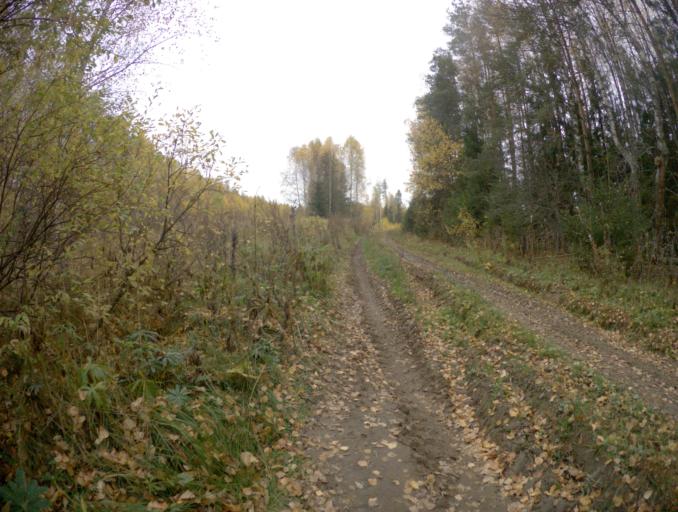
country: RU
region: Vladimir
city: Golovino
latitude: 55.9372
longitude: 40.3706
